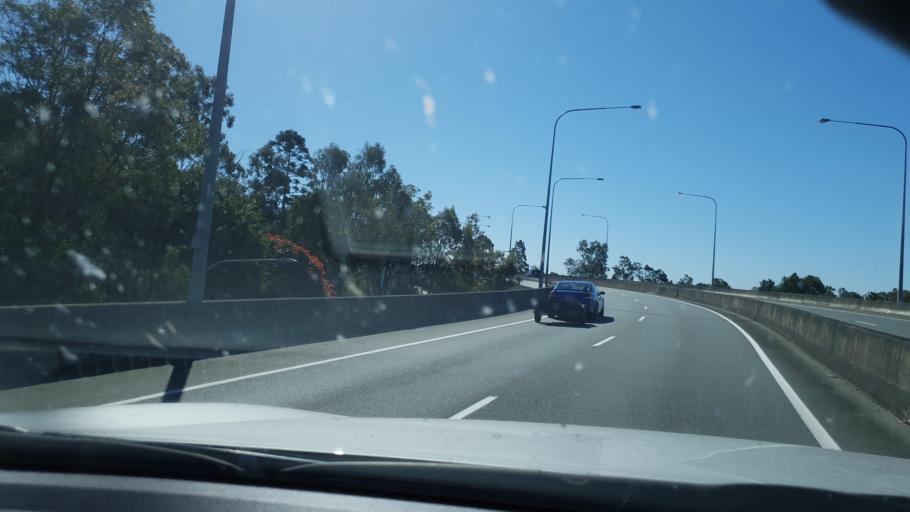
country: AU
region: Queensland
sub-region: Brisbane
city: Everton Park
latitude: -27.3869
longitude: 152.9848
